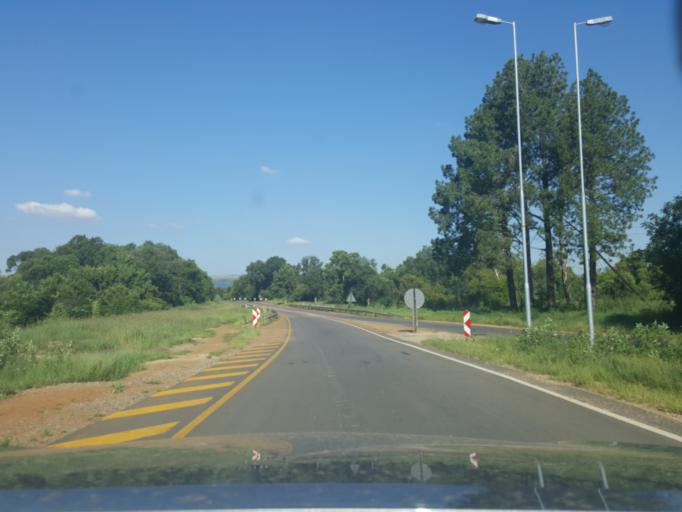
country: ZA
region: Gauteng
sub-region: City of Tshwane Metropolitan Municipality
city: Cullinan
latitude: -25.7545
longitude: 28.3795
